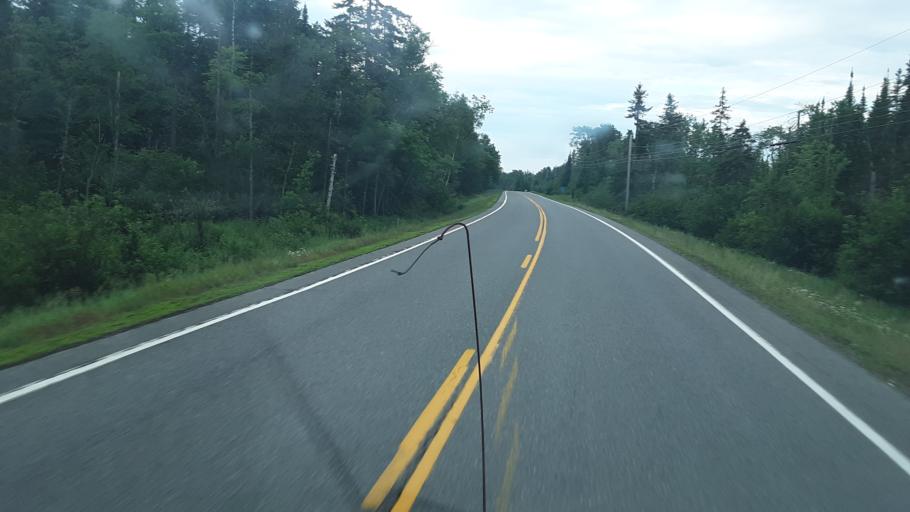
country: US
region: Maine
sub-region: Aroostook County
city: Presque Isle
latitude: 46.4427
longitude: -68.3849
